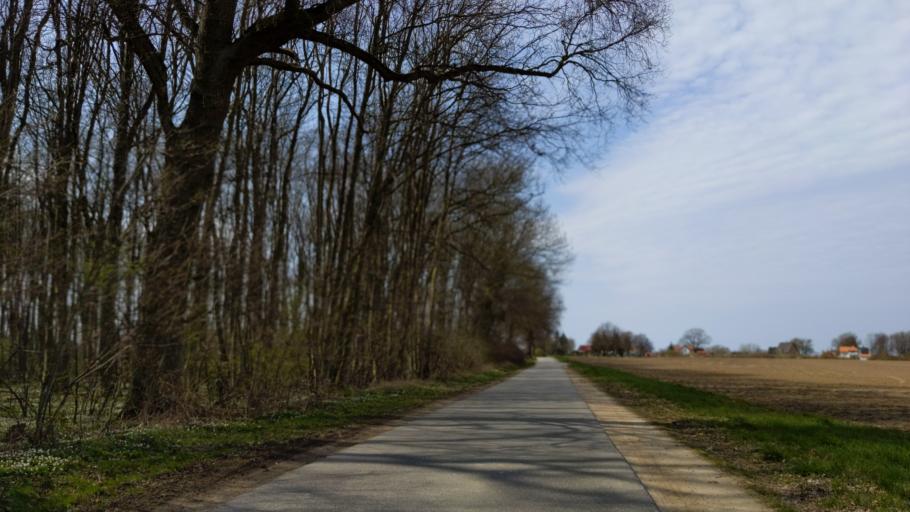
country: DE
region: Mecklenburg-Vorpommern
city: Dassow
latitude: 53.9566
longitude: 10.9468
